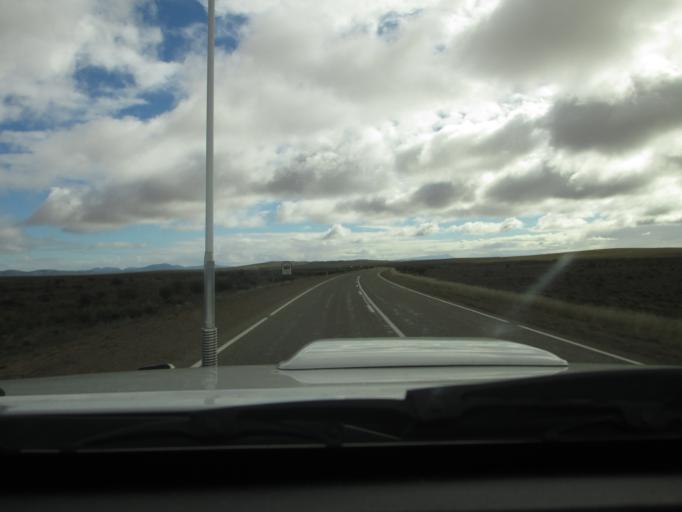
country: AU
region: South Australia
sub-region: Flinders Ranges
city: Quorn
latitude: -32.1191
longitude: 138.5060
